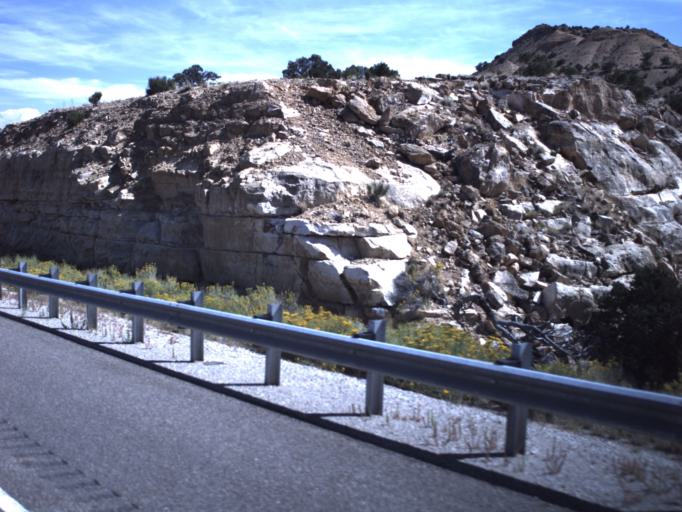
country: US
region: Utah
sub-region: Emery County
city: Castle Dale
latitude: 38.9144
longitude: -110.5135
